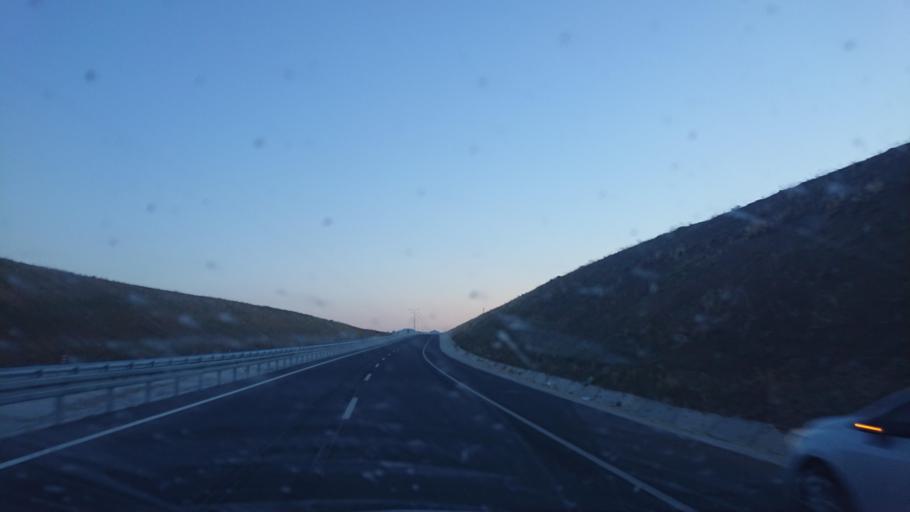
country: TR
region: Aksaray
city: Balci
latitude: 38.7811
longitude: 34.1161
